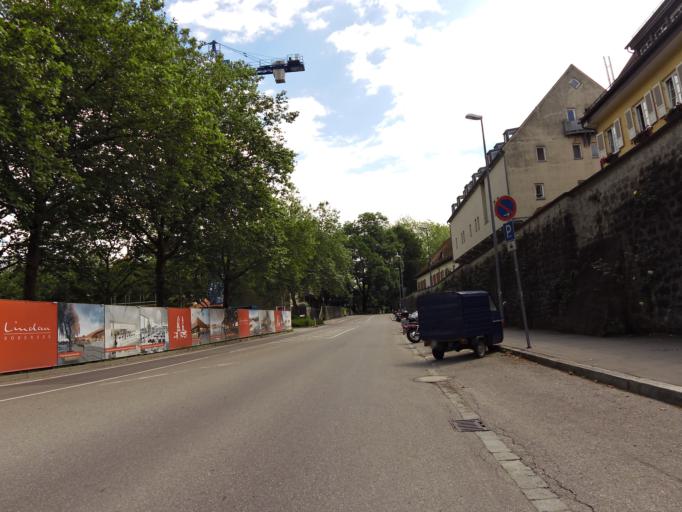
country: DE
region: Bavaria
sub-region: Swabia
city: Lindau
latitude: 47.5481
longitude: 9.6865
